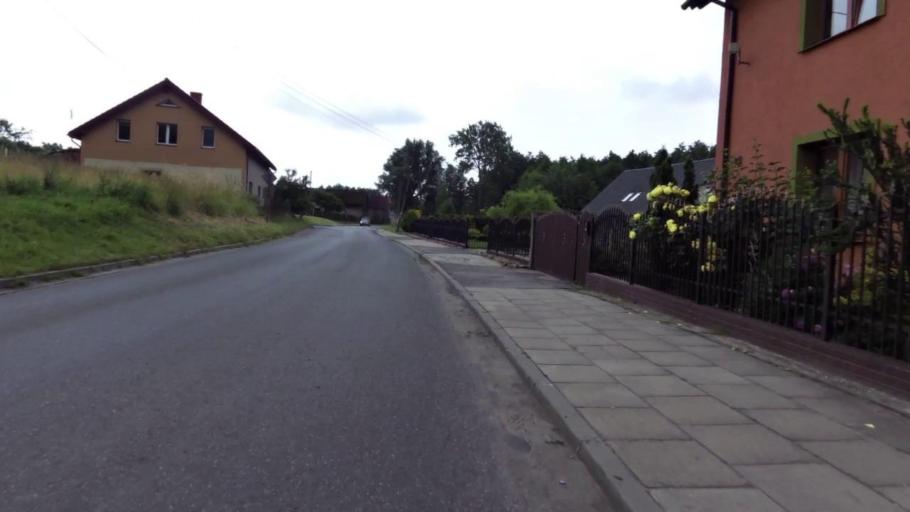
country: PL
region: West Pomeranian Voivodeship
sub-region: Powiat kamienski
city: Wolin
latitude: 53.8392
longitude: 14.6253
